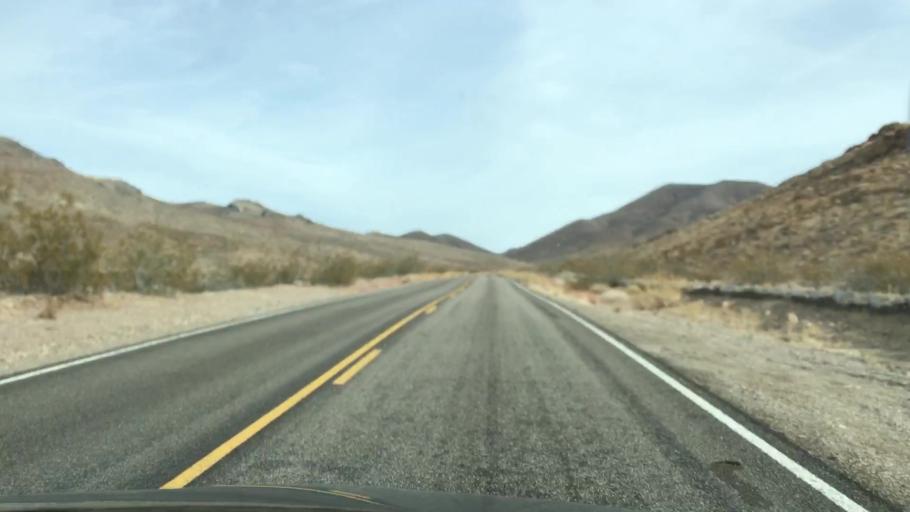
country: US
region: Nevada
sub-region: Nye County
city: Beatty
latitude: 36.7521
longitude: -116.9359
